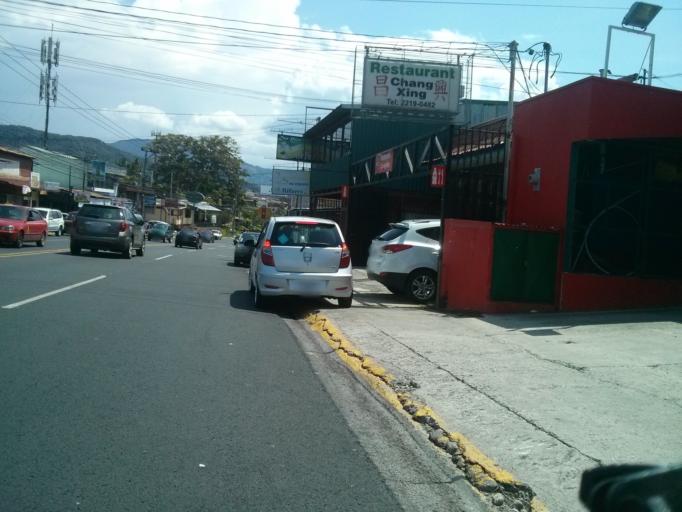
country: CR
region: San Jose
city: San Pedro
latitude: 9.9068
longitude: -84.0568
